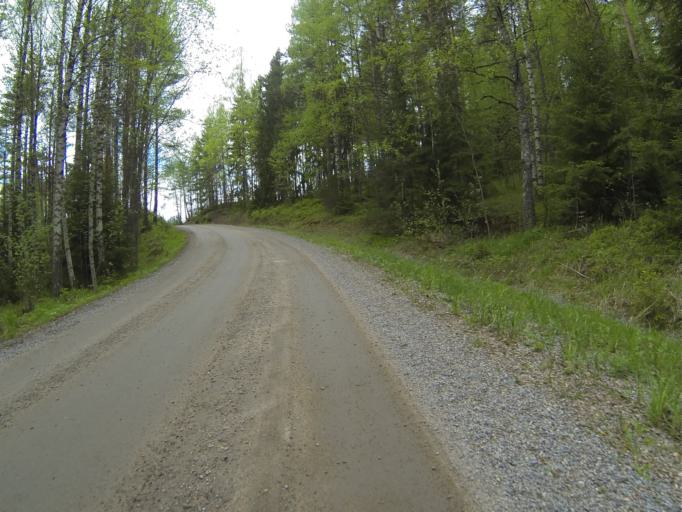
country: FI
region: Varsinais-Suomi
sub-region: Salo
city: Halikko
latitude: 60.3426
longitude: 23.0888
